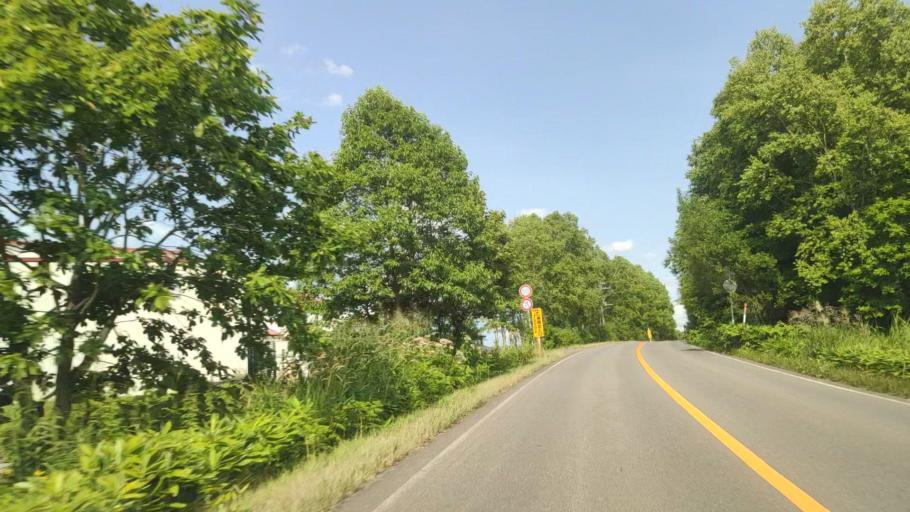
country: JP
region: Hokkaido
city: Nayoro
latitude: 44.2811
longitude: 142.4251
